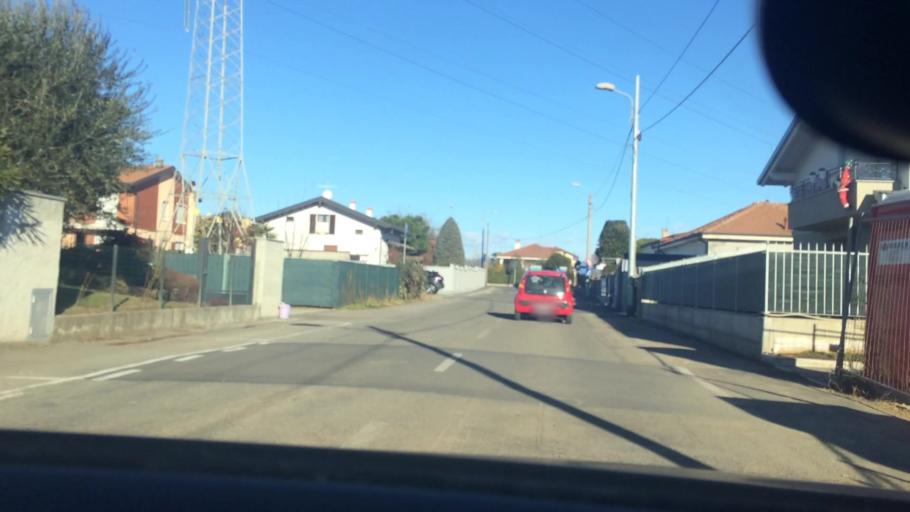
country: IT
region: Lombardy
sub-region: Provincia di Monza e Brianza
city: Ceriano Laghetto
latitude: 45.6278
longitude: 9.0712
